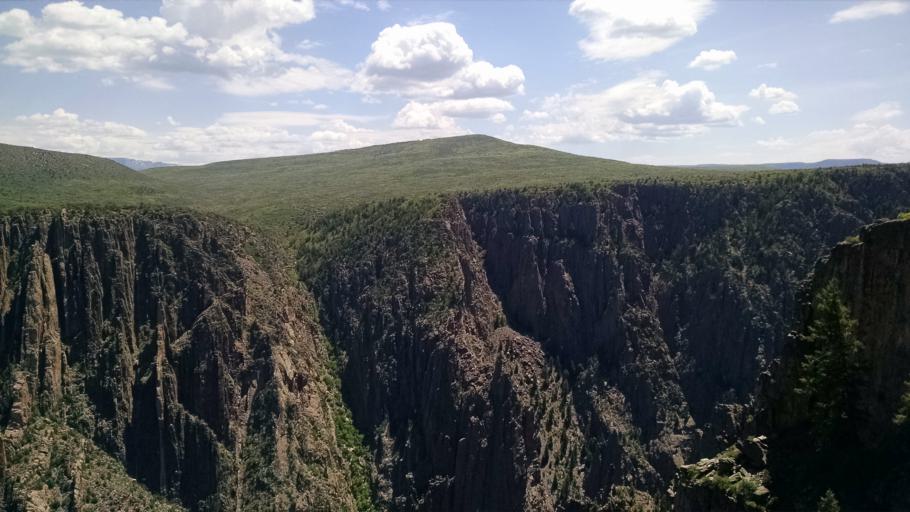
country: US
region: Colorado
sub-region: Montrose County
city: Montrose
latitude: 38.5557
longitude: -107.6864
